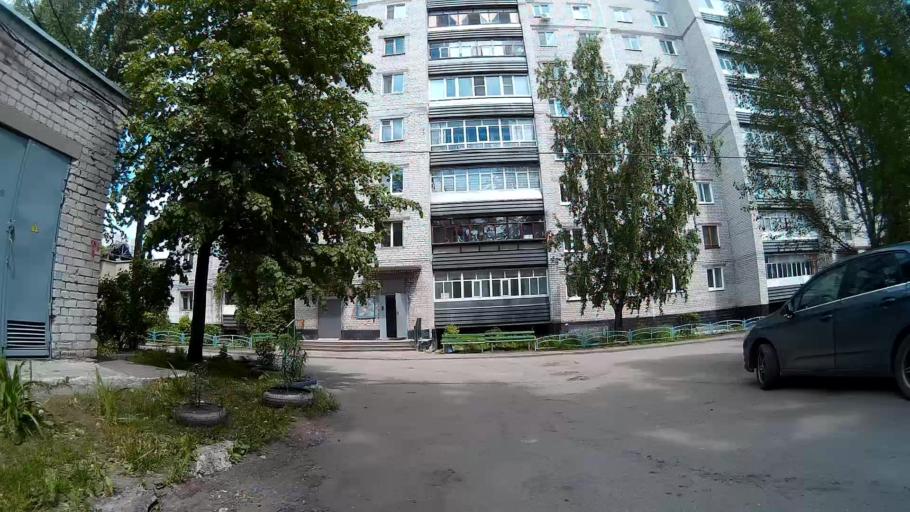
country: RU
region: Ulyanovsk
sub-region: Ulyanovskiy Rayon
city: Ulyanovsk
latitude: 54.2894
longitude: 48.3694
